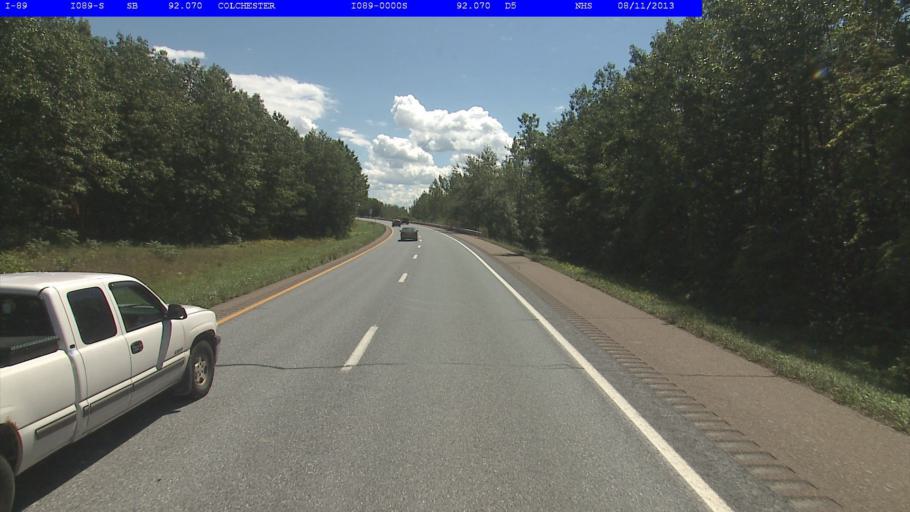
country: US
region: Vermont
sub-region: Chittenden County
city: Winooski
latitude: 44.5108
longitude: -73.1910
